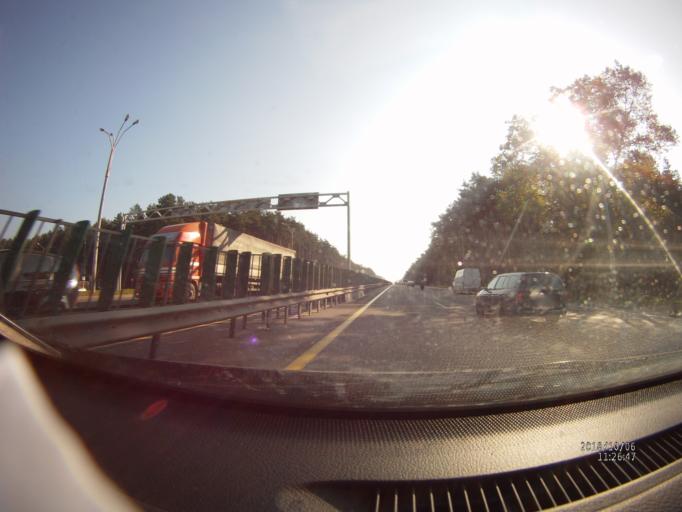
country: BY
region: Minsk
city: Borovlyany
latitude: 53.9578
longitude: 27.6327
